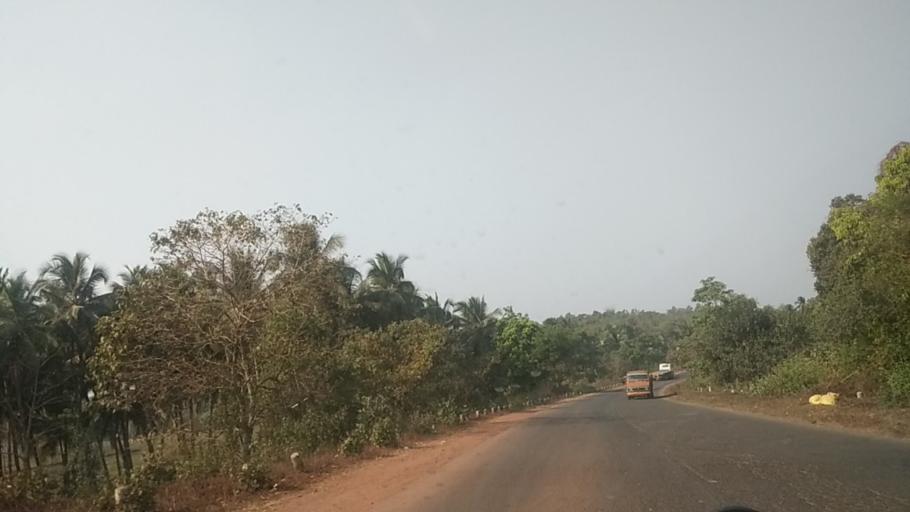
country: IN
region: Goa
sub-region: North Goa
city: Colovale
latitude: 15.6709
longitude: 73.8371
